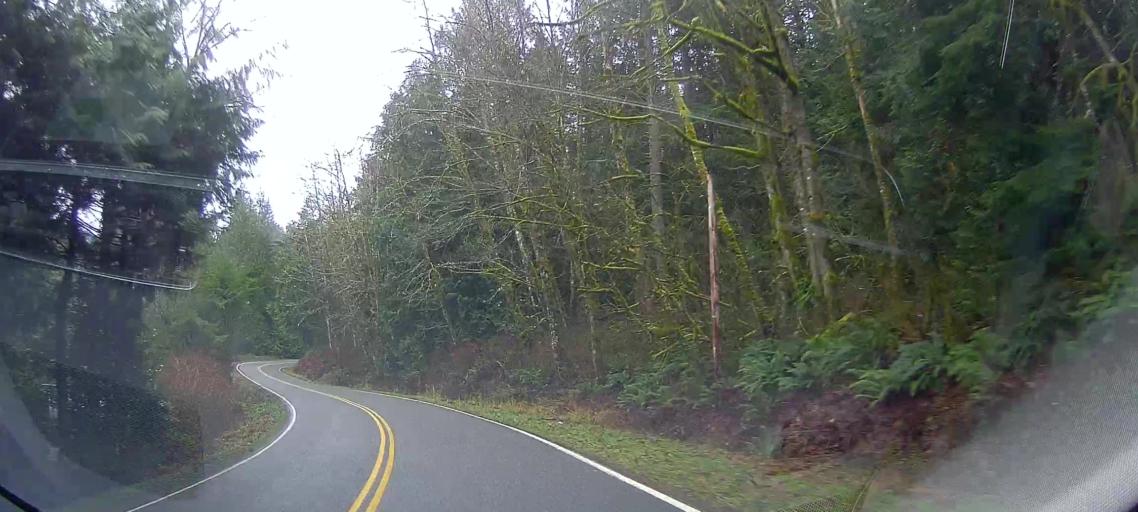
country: US
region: Washington
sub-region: Whatcom County
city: Sudden Valley
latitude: 48.6729
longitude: -122.2851
